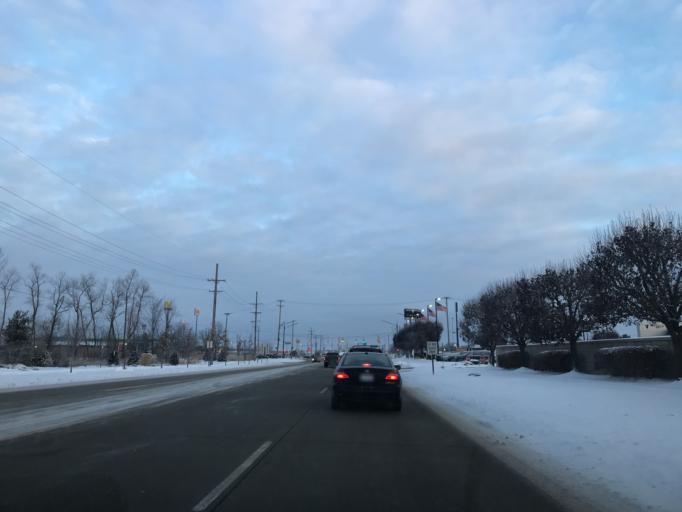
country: US
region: Michigan
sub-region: Oakland County
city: Wixom
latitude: 42.4924
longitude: -83.5356
